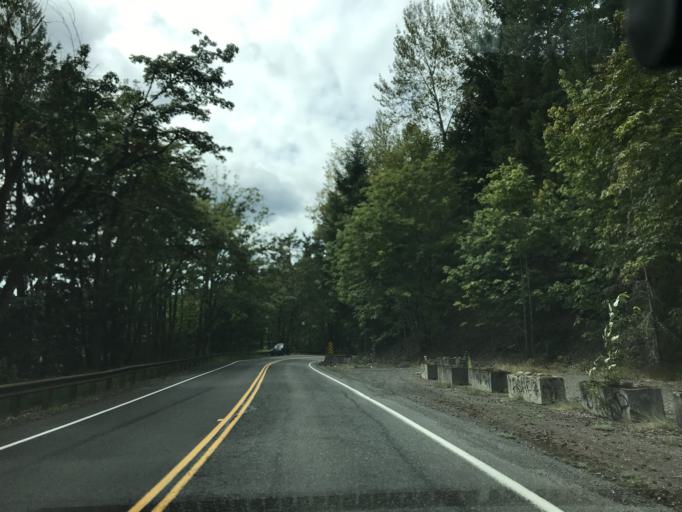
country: US
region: Washington
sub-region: King County
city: Black Diamond
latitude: 47.2858
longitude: -122.0267
